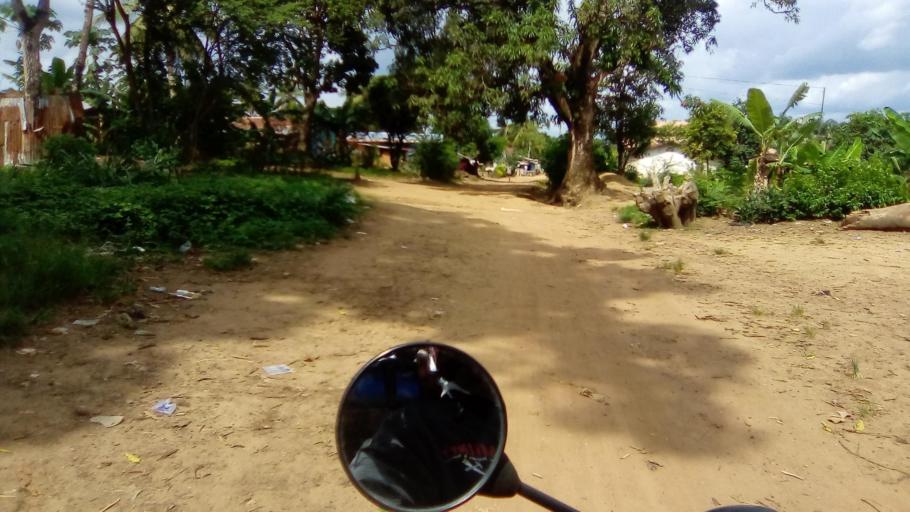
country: SL
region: Southern Province
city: Bo
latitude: 7.9515
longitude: -11.7280
